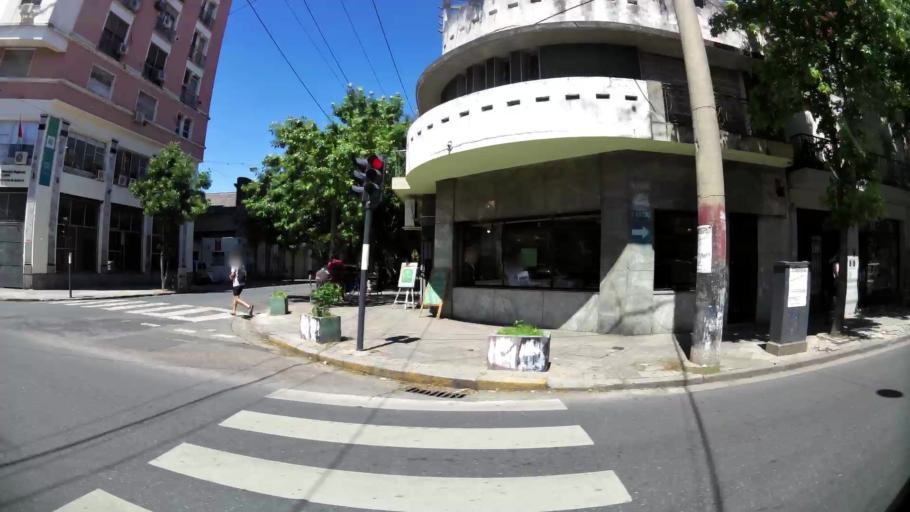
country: AR
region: Santa Fe
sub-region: Departamento de Rosario
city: Rosario
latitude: -32.9402
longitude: -60.6609
